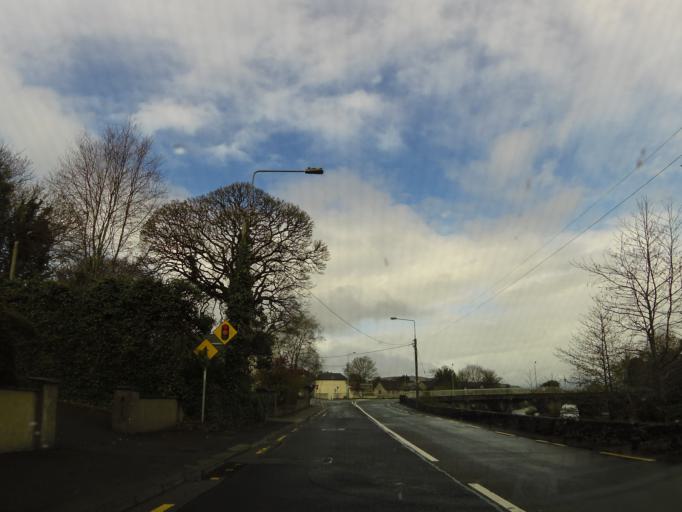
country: IE
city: Ballisodare
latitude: 54.2086
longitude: -8.5088
